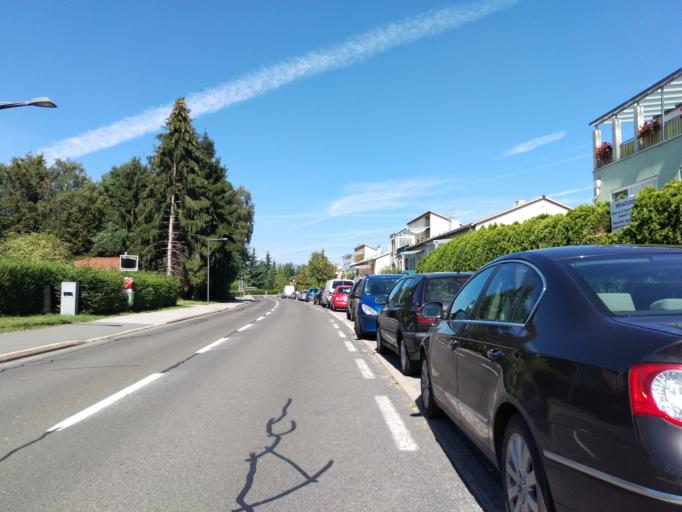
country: AT
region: Styria
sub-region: Politischer Bezirk Graz-Umgebung
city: Nestelbach bei Graz
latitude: 47.0793
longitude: 15.5810
